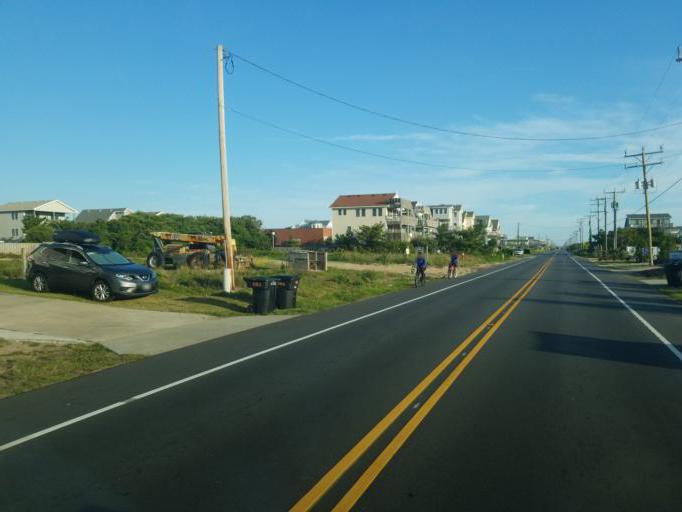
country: US
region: North Carolina
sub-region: Dare County
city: Kill Devil Hills
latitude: 36.0226
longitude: -75.6624
